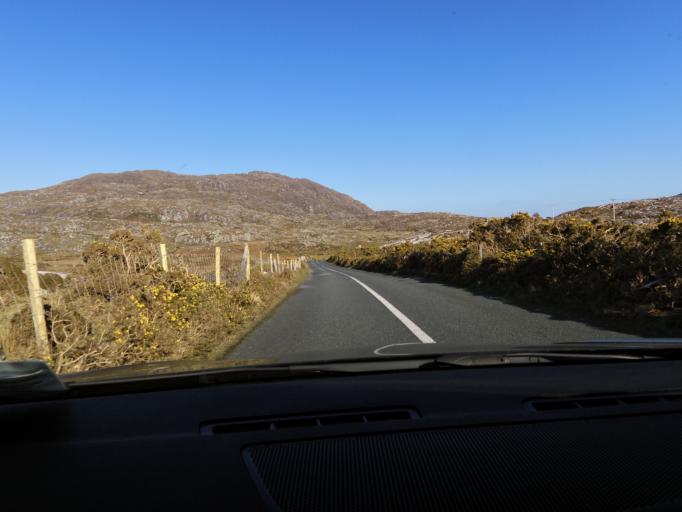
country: IE
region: Connaught
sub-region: County Galway
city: Clifden
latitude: 53.3927
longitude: -9.9851
